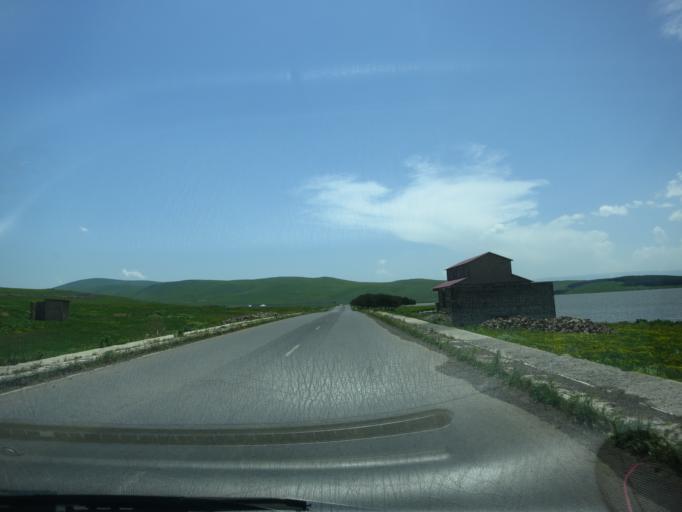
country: GE
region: Samtskhe-Javakheti
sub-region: Ninotsminda
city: Ninotsminda
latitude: 41.3058
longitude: 43.7604
